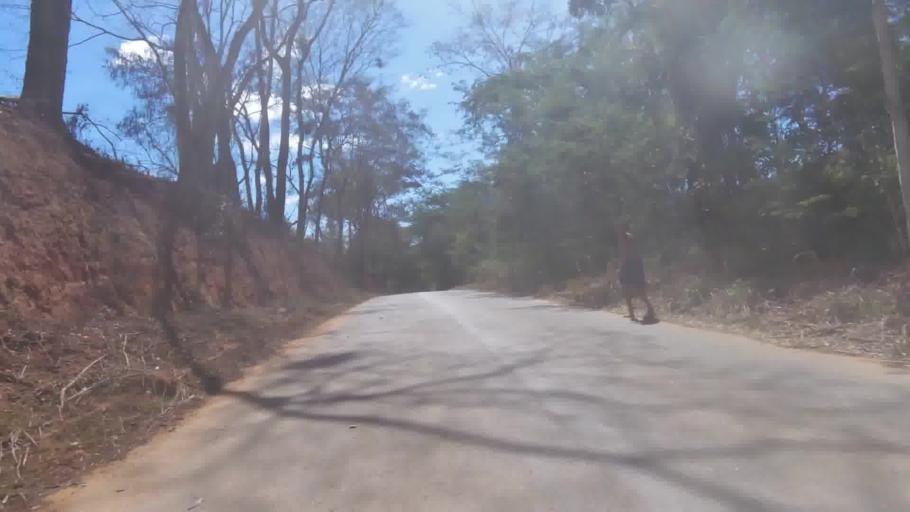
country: BR
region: Espirito Santo
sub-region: Cachoeiro De Itapemirim
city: Cachoeiro de Itapemirim
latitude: -20.9301
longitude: -41.2134
